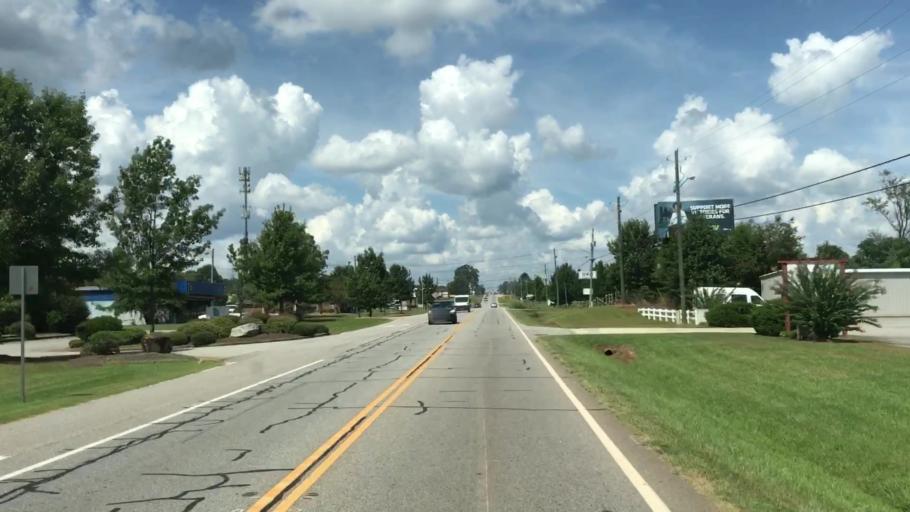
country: US
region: Georgia
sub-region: Oconee County
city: Watkinsville
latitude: 33.8527
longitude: -83.3984
